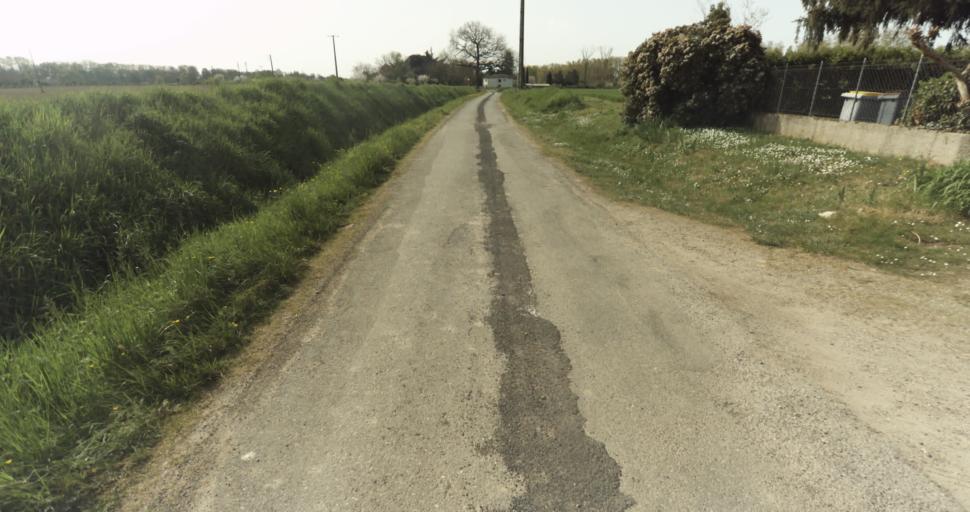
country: FR
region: Midi-Pyrenees
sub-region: Departement du Tarn-et-Garonne
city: Moissac
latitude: 44.0862
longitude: 1.0927
